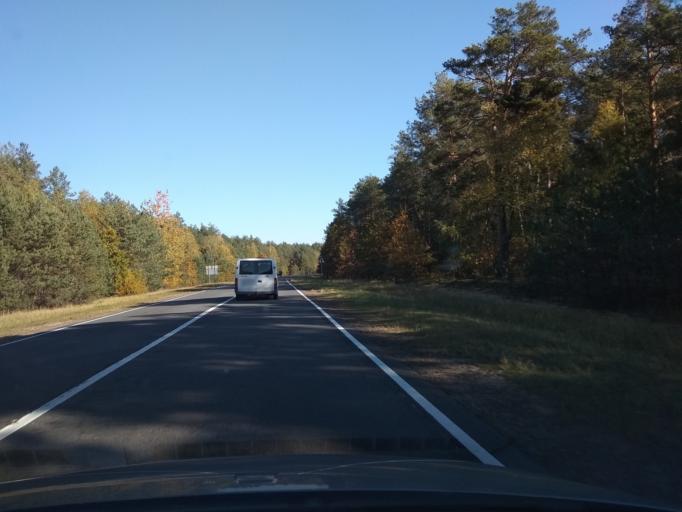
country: BY
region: Brest
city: Kobryn
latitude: 52.0238
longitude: 24.2472
